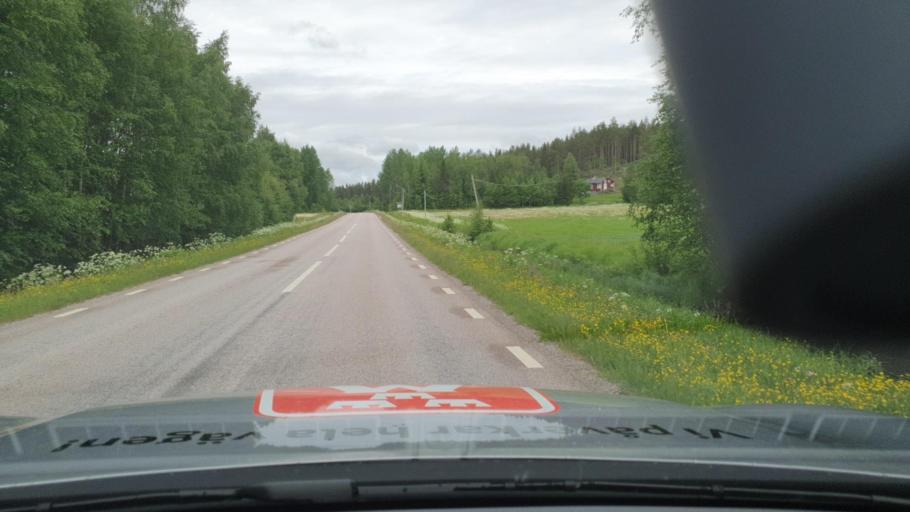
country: SE
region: Norrbotten
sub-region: Lulea Kommun
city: Ranea
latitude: 65.8809
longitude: 22.2726
